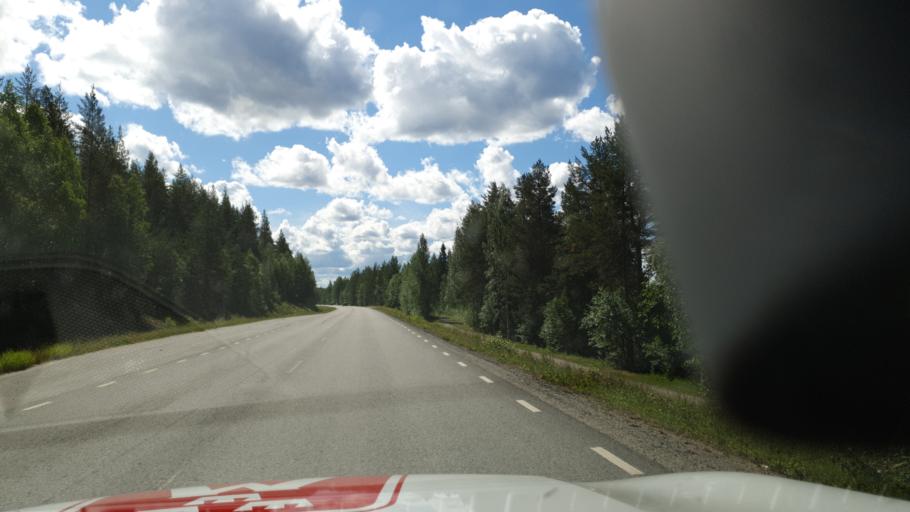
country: SE
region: Vaesterbotten
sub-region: Lycksele Kommun
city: Lycksele
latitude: 64.6276
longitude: 18.6818
